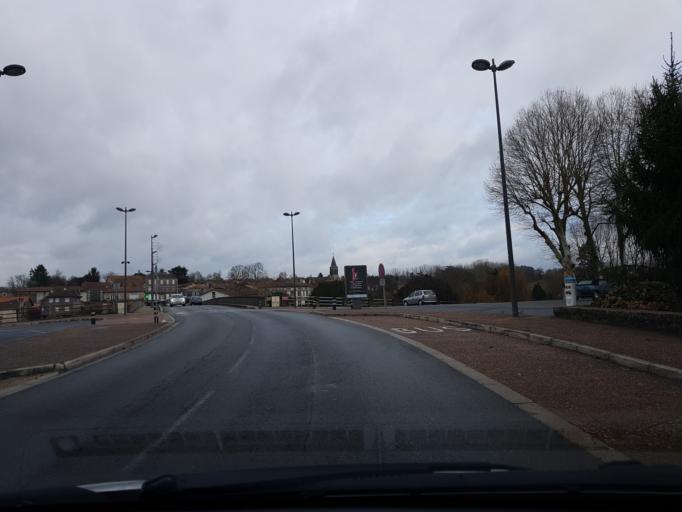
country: FR
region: Poitou-Charentes
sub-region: Departement de la Charente
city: Chabanais
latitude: 45.8741
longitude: 0.7196
